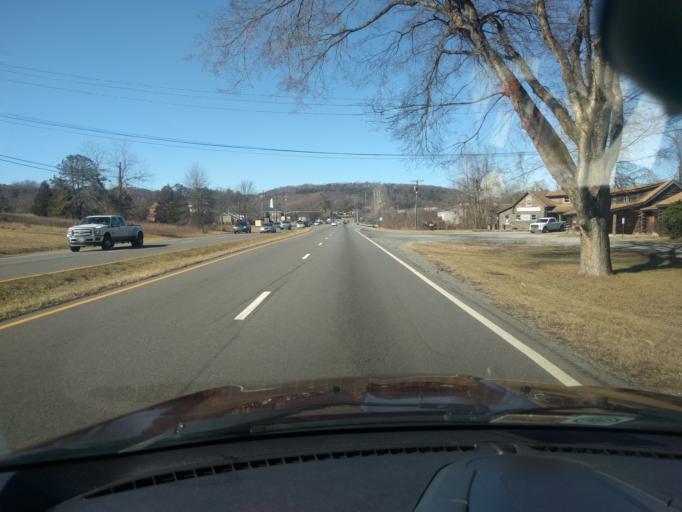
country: US
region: Virginia
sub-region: Roanoke County
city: Narrows
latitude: 37.2018
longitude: -79.9475
